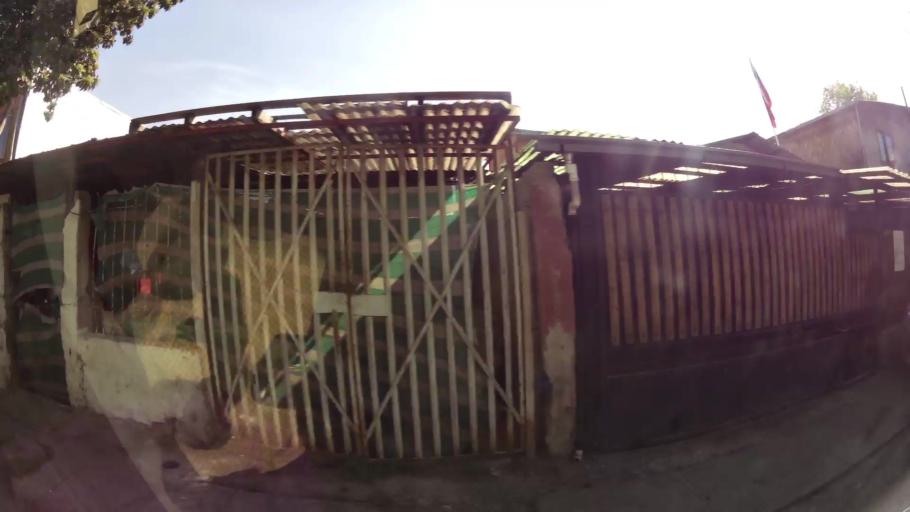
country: CL
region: Santiago Metropolitan
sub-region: Provincia de Santiago
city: Lo Prado
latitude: -33.4316
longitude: -70.7435
